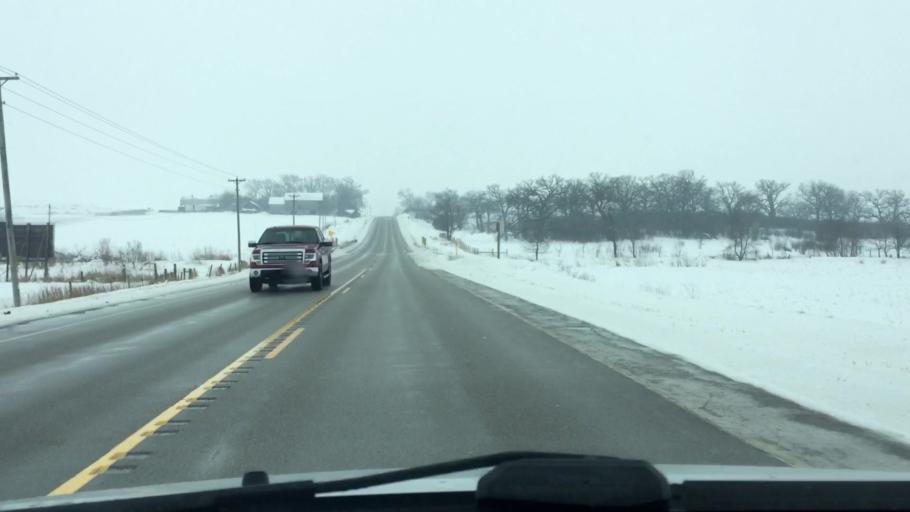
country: US
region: Wisconsin
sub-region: Walworth County
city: Lake Geneva
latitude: 42.5322
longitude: -88.4429
